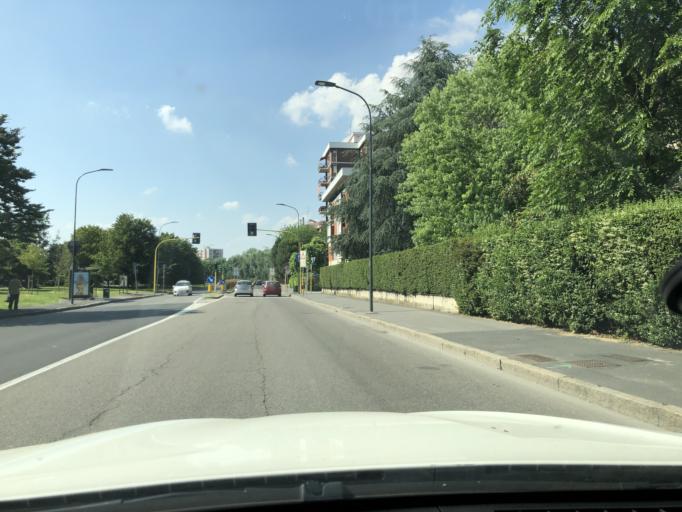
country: IT
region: Lombardy
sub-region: Citta metropolitana di Milano
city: Novate Milanese
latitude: 45.5150
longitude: 9.1571
